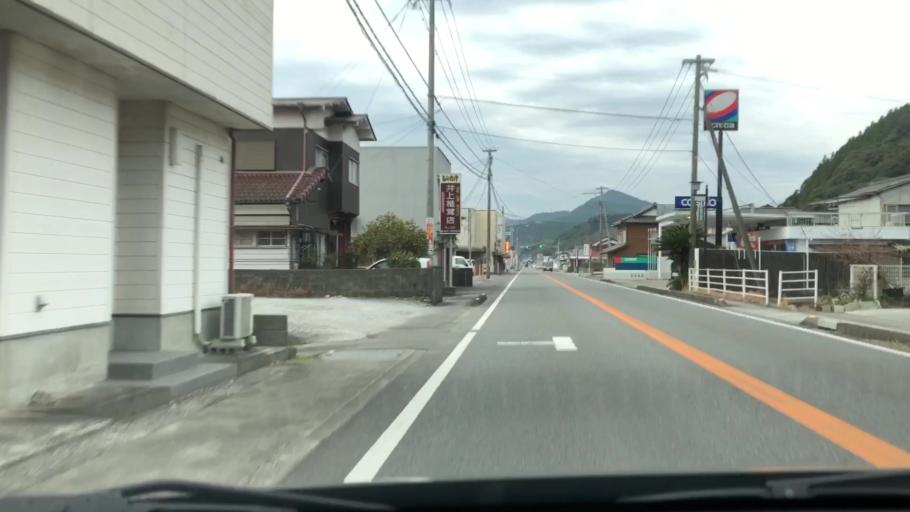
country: JP
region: Oita
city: Saiki
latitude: 32.9758
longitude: 131.8443
